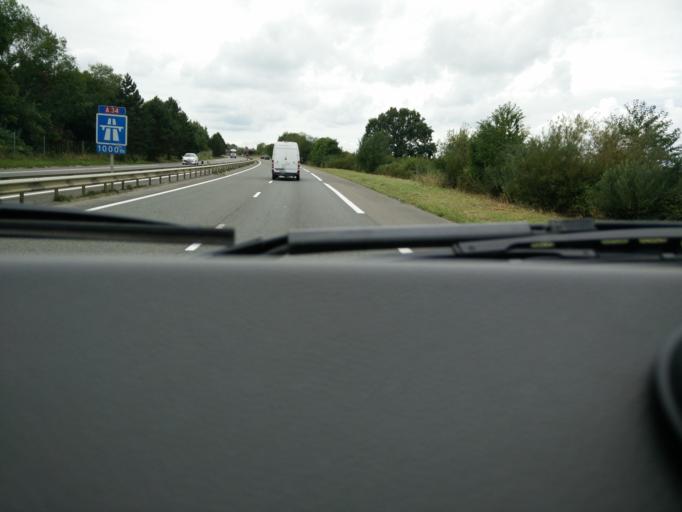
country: FR
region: Champagne-Ardenne
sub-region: Departement des Ardennes
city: Sedan
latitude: 49.6907
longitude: 4.9236
